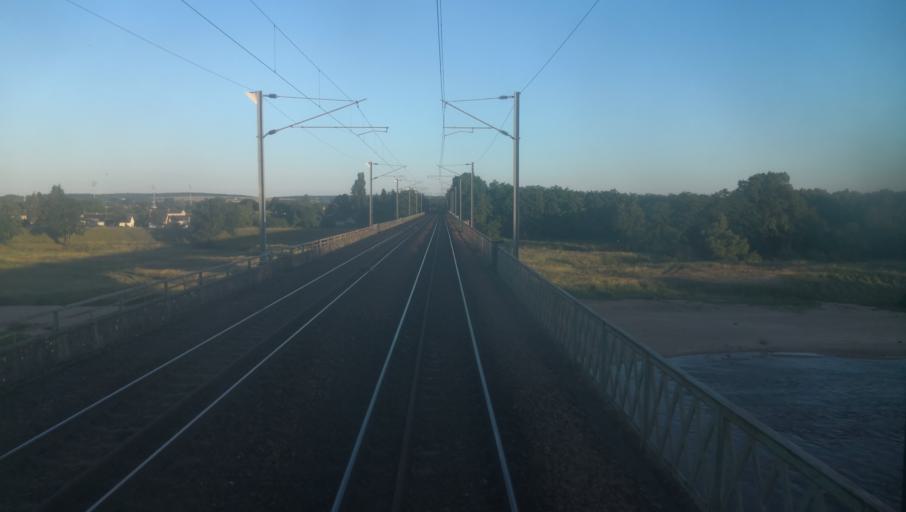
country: FR
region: Bourgogne
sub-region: Departement de la Nievre
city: Nevers
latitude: 46.9827
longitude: 3.1522
